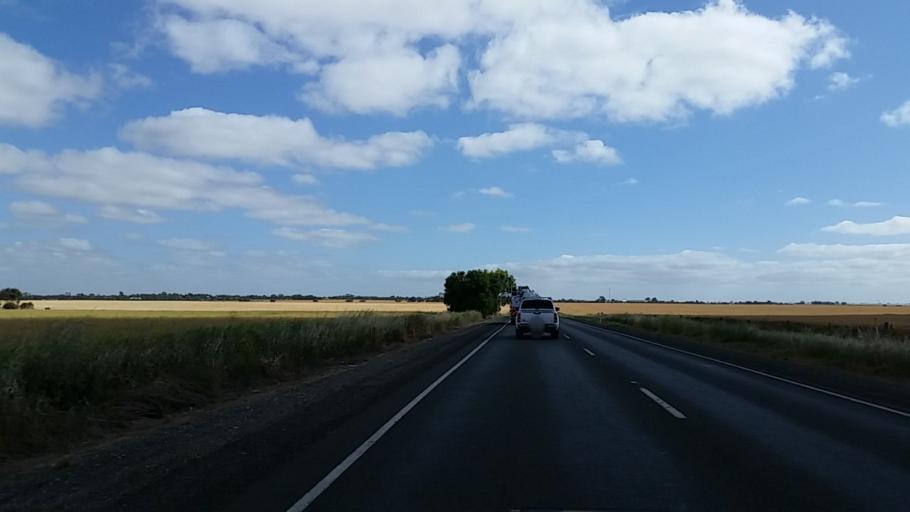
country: AU
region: South Australia
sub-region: Light
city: Willaston
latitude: -34.5602
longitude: 138.7472
